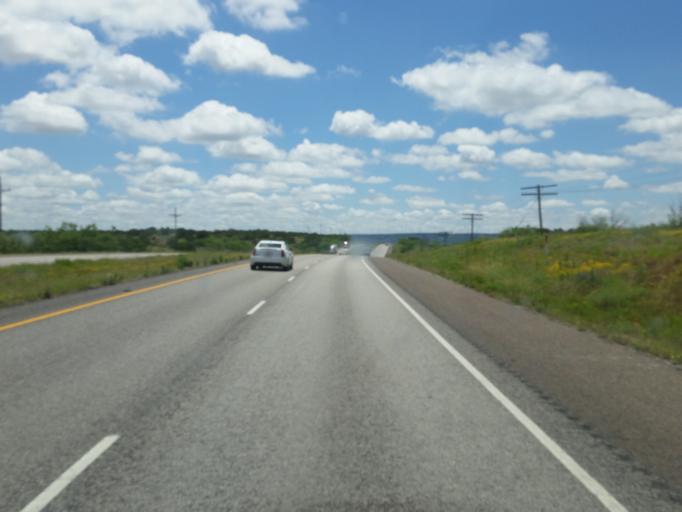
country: US
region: Texas
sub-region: Garza County
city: Post
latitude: 33.0264
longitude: -101.1848
